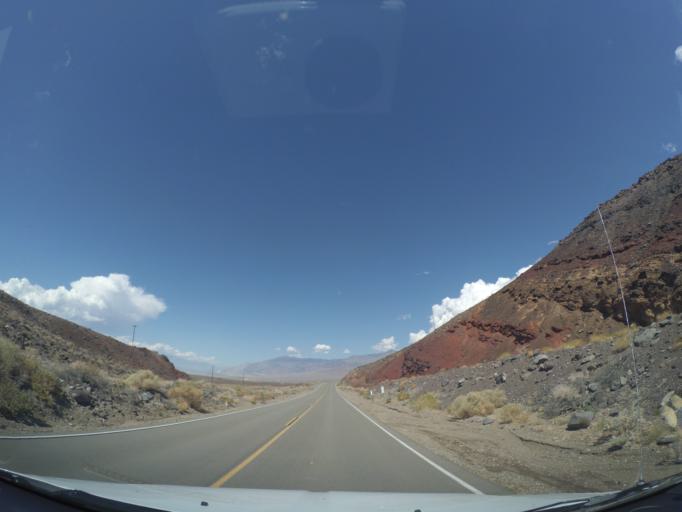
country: US
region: California
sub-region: Inyo County
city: Lone Pine
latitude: 36.3903
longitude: -117.8068
